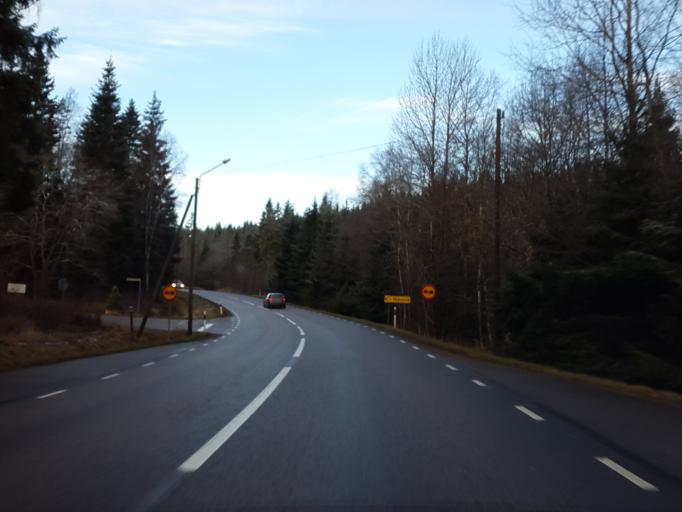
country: SE
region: Vaestra Goetaland
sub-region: Boras Kommun
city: Sjomarken
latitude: 57.7552
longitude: 12.8785
